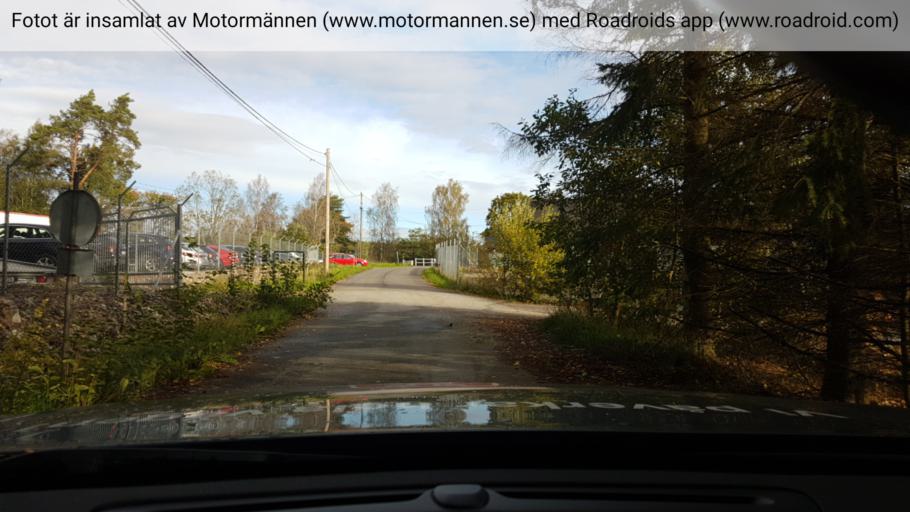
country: SE
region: Stockholm
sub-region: Vallentuna Kommun
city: Vallentuna
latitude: 59.6500
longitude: 18.0240
